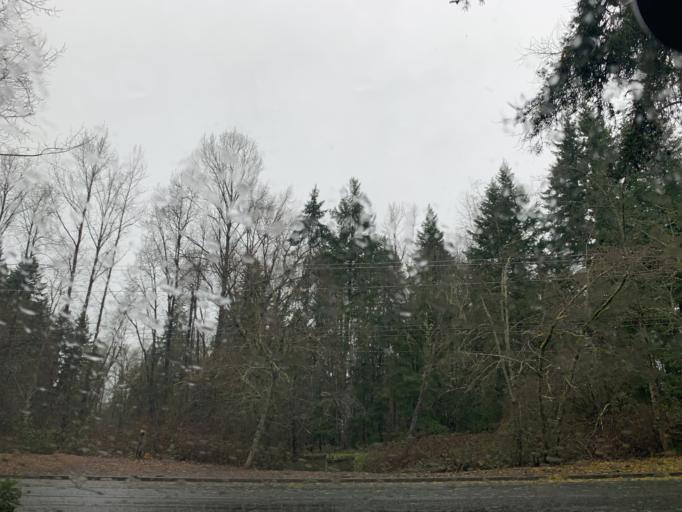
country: US
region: Washington
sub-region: King County
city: Kingsgate
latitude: 47.7372
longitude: -122.1774
